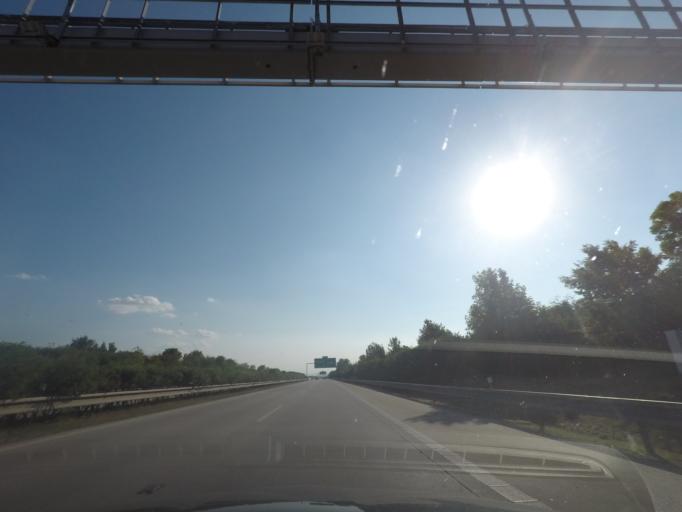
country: CZ
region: Olomoucky
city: Velky Tynec
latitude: 49.5687
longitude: 17.3392
